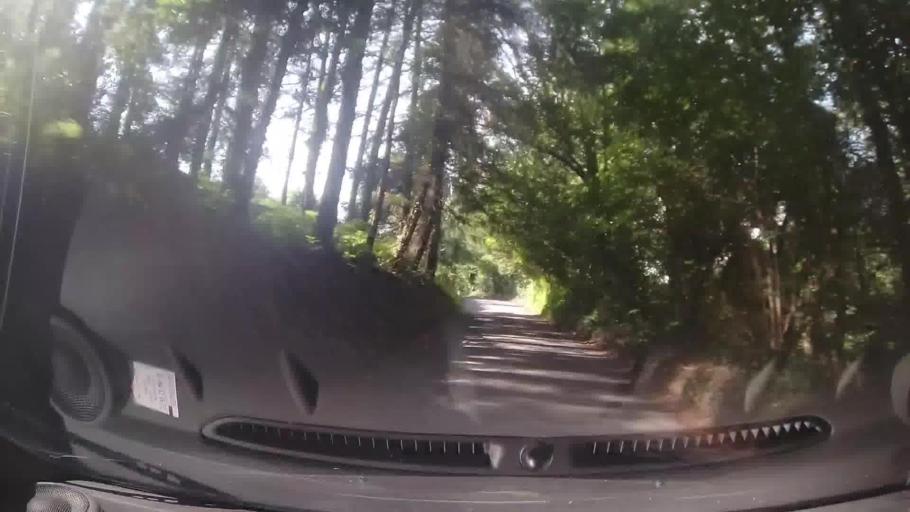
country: GB
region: Wales
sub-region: Pembrokeshire
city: Saundersfoot
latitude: 51.7447
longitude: -4.6774
